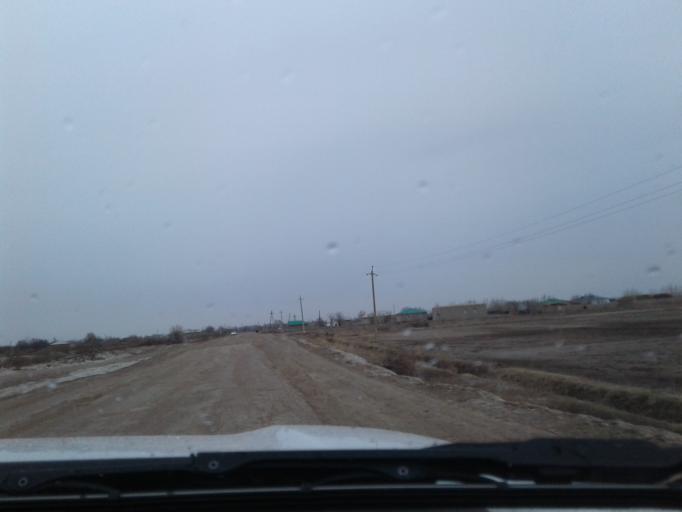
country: UZ
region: Karakalpakstan
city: Shumanay Shahri
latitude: 42.2798
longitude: 58.6454
